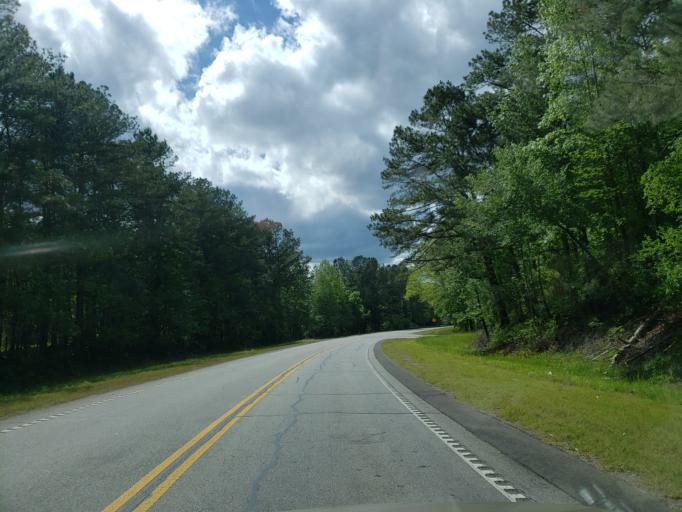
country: US
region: Georgia
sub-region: Haralson County
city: Tallapoosa
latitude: 33.7402
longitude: -85.3329
